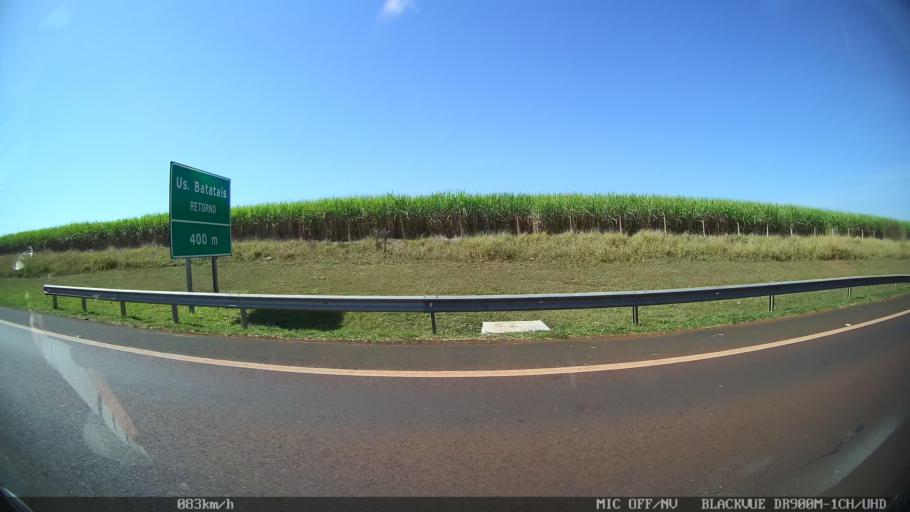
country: BR
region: Sao Paulo
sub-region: Batatais
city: Batatais
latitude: -20.8366
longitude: -47.6012
